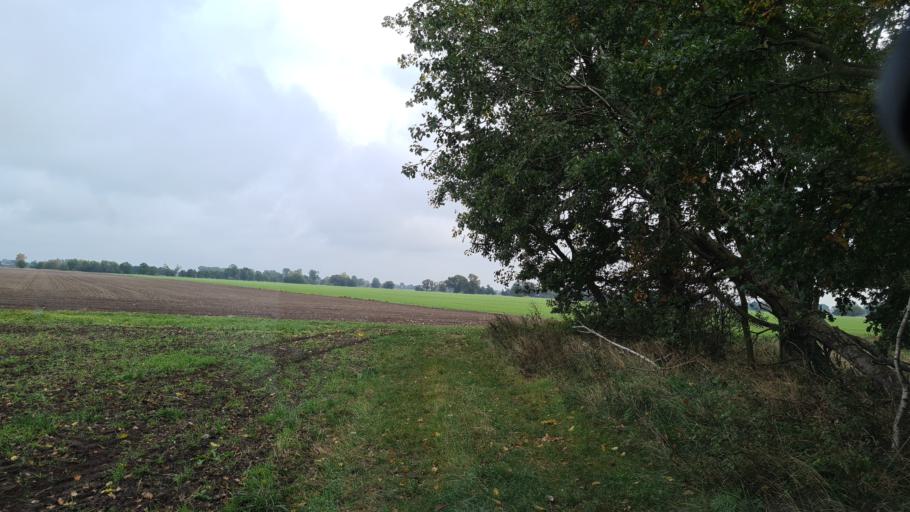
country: DE
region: Brandenburg
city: Schonewalde
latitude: 51.6820
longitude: 13.5693
